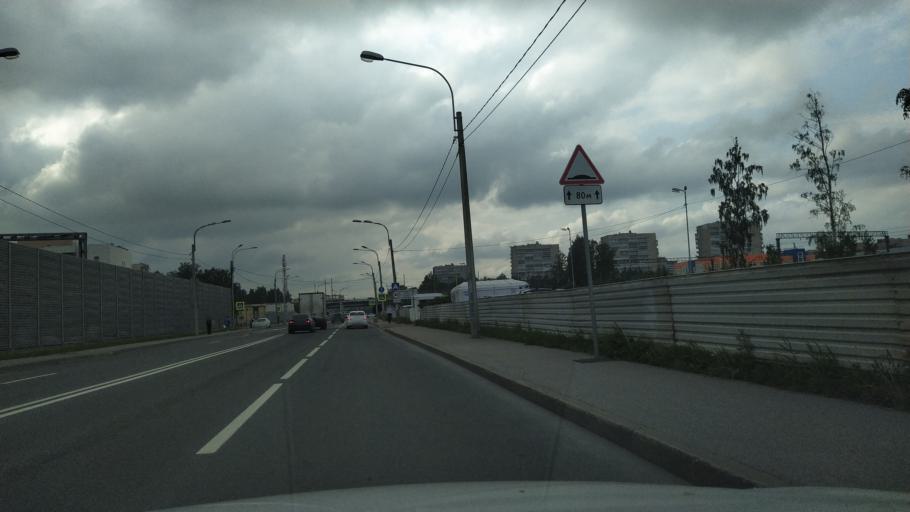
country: RU
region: St.-Petersburg
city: Krasnogvargeisky
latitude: 59.9862
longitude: 30.4342
